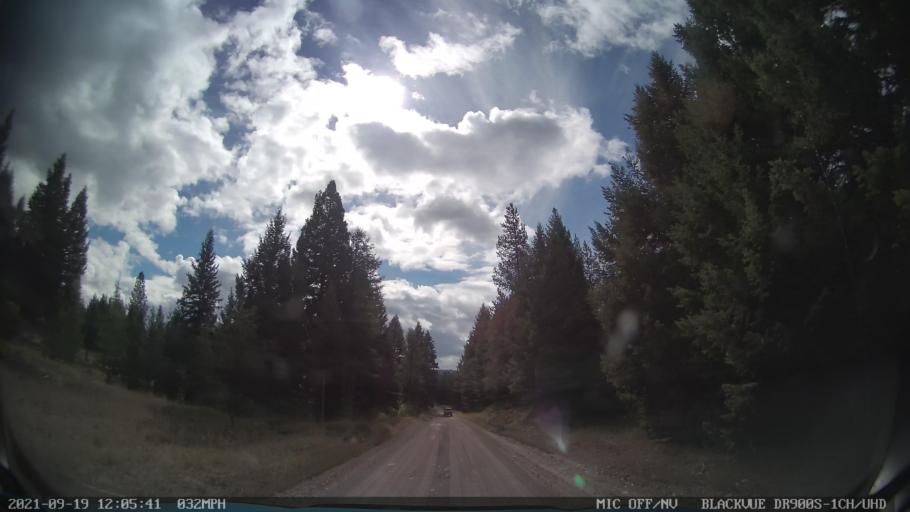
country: US
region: Montana
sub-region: Missoula County
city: Seeley Lake
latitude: 47.1899
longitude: -113.4238
